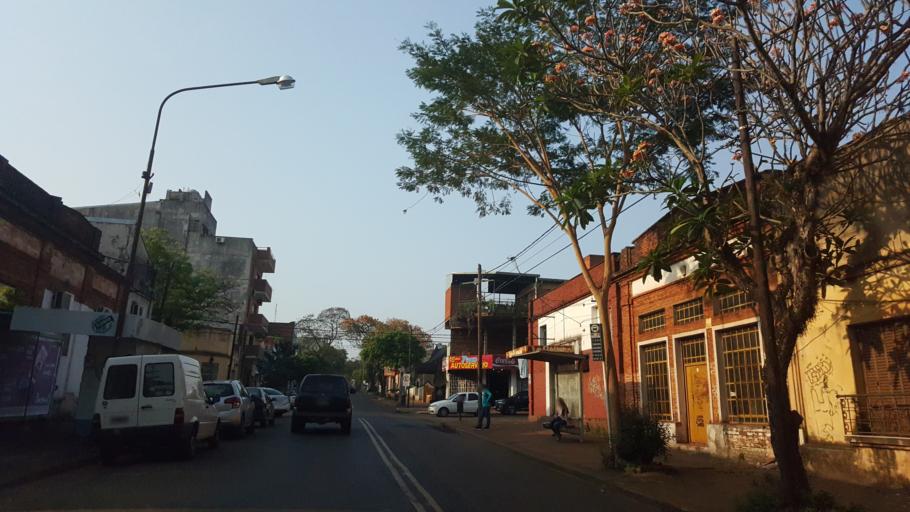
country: AR
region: Misiones
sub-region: Departamento de Capital
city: Posadas
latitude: -27.3713
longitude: -55.8931
